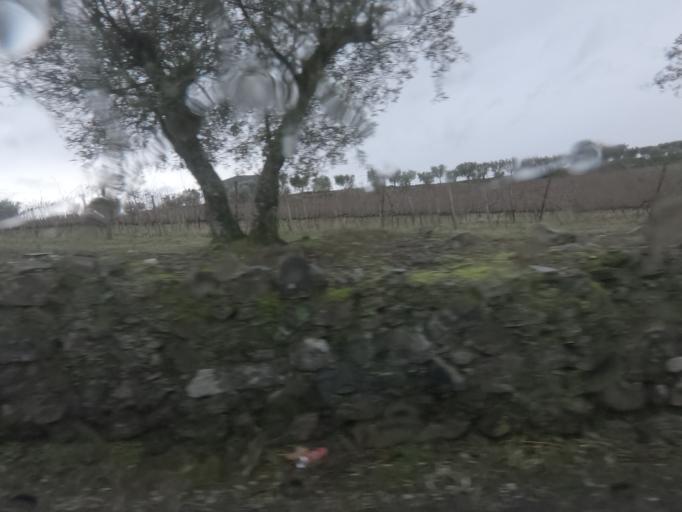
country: PT
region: Vila Real
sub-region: Peso da Regua
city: Peso da Regua
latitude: 41.1651
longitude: -7.7344
